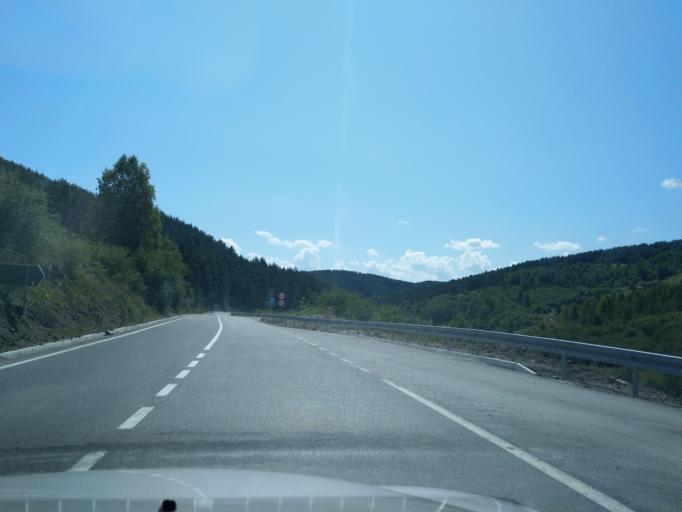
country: RS
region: Central Serbia
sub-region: Zlatiborski Okrug
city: Sjenica
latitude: 43.2866
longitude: 19.9442
